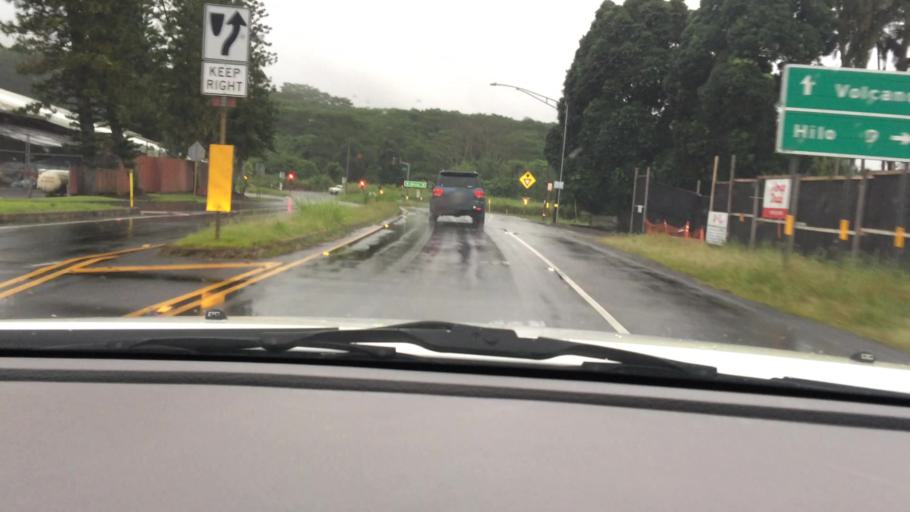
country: US
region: Hawaii
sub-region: Hawaii County
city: Kea'au
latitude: 19.6228
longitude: -155.0395
